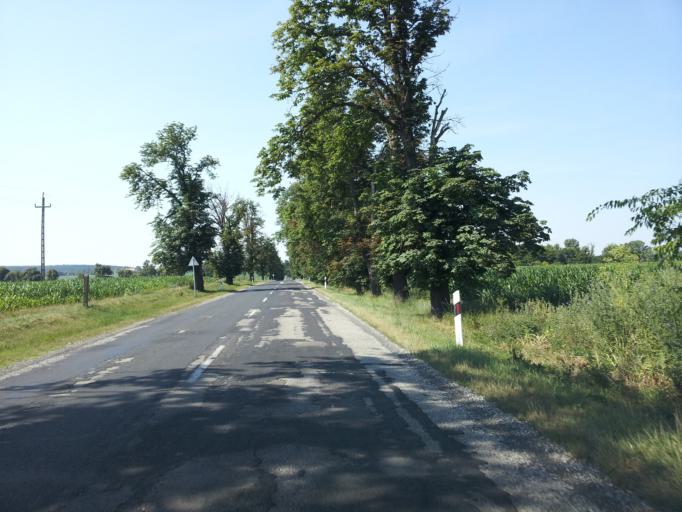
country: HU
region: Fejer
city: Lovasbereny
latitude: 47.2994
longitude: 18.5368
